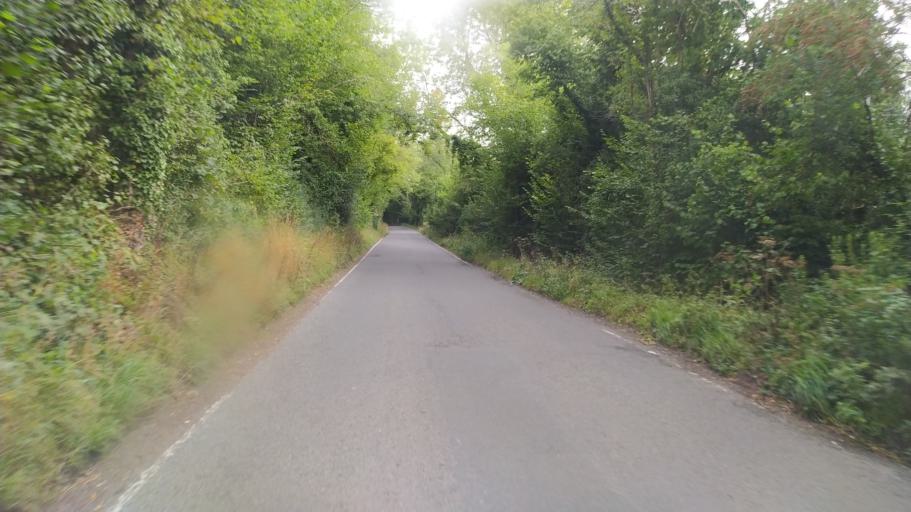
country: GB
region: England
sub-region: Hampshire
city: Four Marks
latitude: 51.0008
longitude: -1.0446
